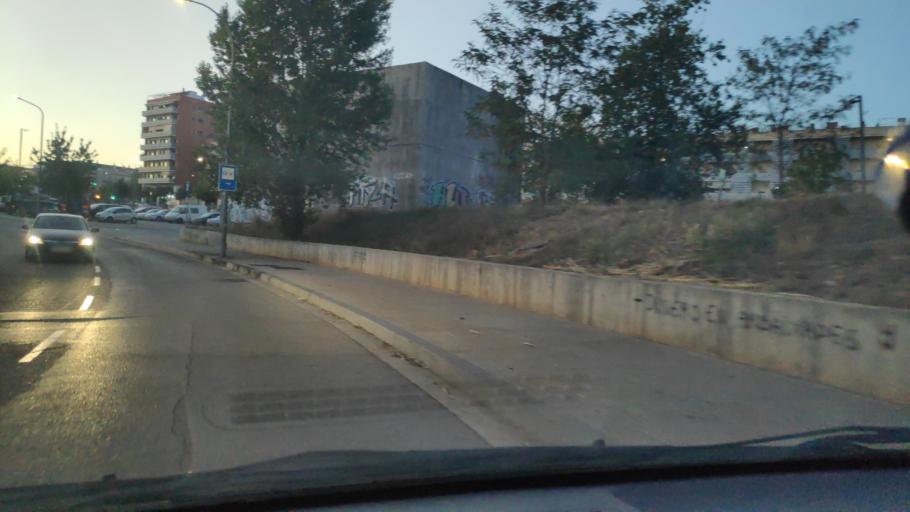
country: ES
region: Catalonia
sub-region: Provincia de Barcelona
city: Terrassa
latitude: 41.5668
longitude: 2.0413
